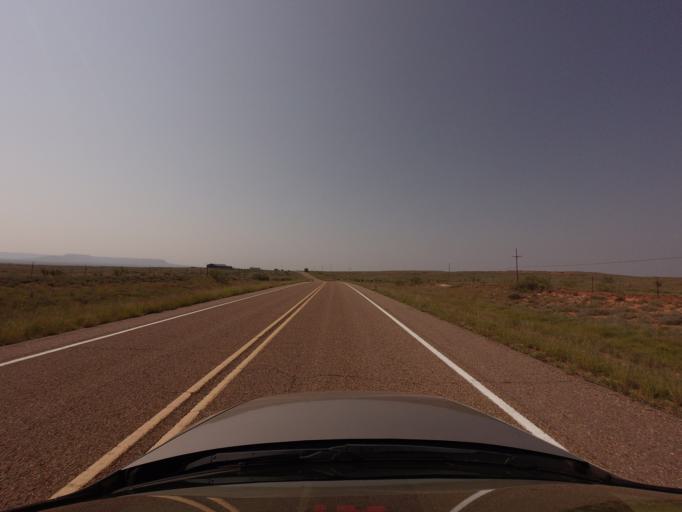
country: US
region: New Mexico
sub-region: Quay County
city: Tucumcari
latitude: 35.1012
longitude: -103.7361
